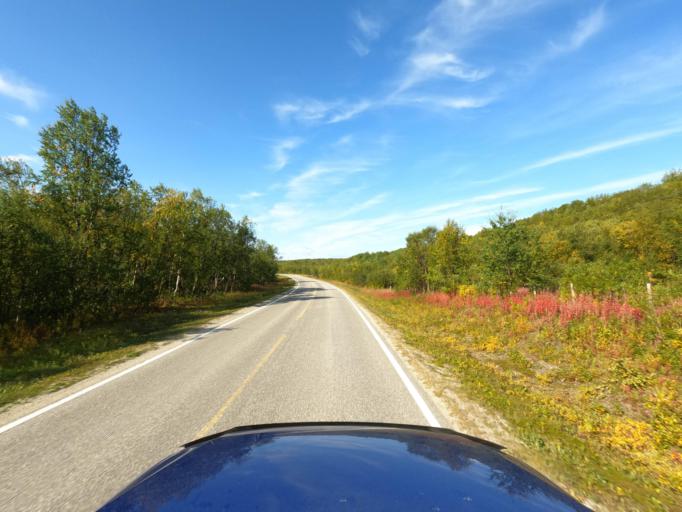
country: NO
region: Finnmark Fylke
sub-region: Porsanger
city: Lakselv
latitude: 69.7619
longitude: 25.2018
